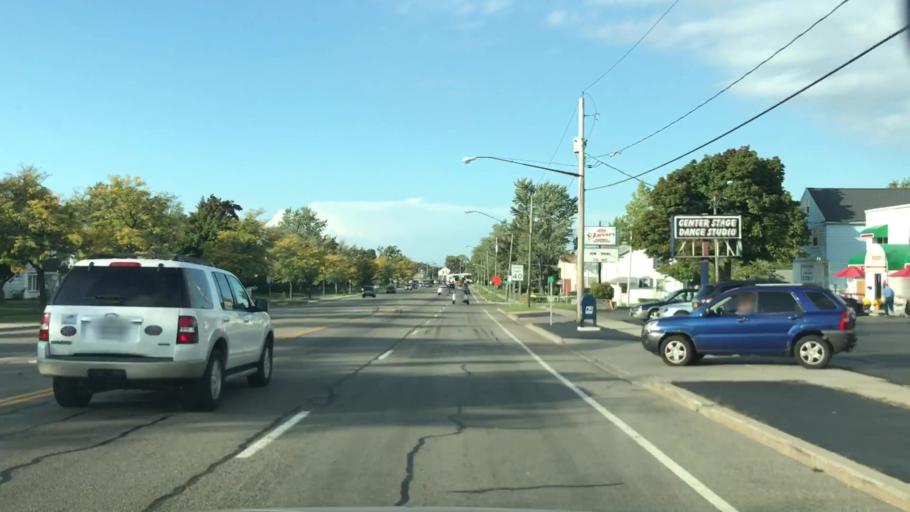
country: US
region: New York
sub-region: Erie County
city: Williamsville
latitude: 42.9455
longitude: -78.7543
